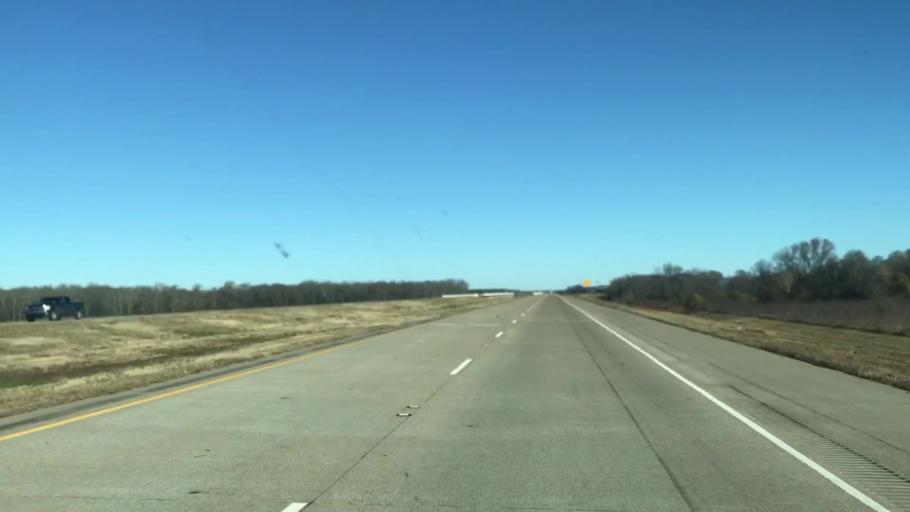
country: US
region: Louisiana
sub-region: Caddo Parish
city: Blanchard
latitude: 32.6205
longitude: -93.8356
